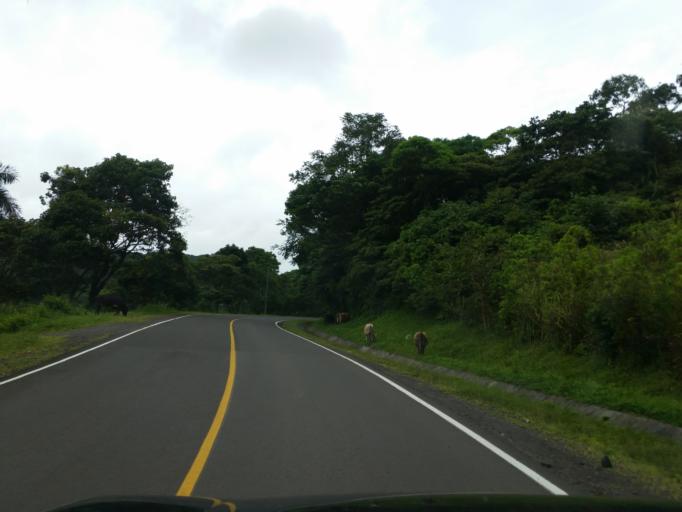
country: NI
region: Matagalpa
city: San Ramon
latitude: 12.9681
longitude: -85.8530
